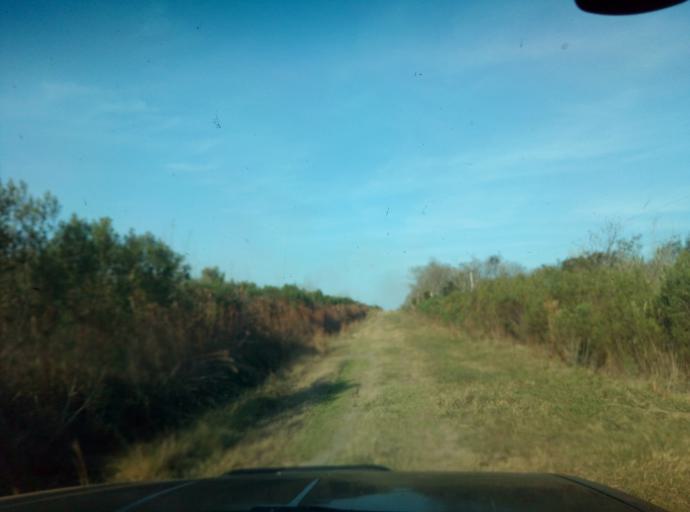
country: PY
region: Caaguazu
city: Doctor Cecilio Baez
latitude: -25.1999
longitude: -56.1246
